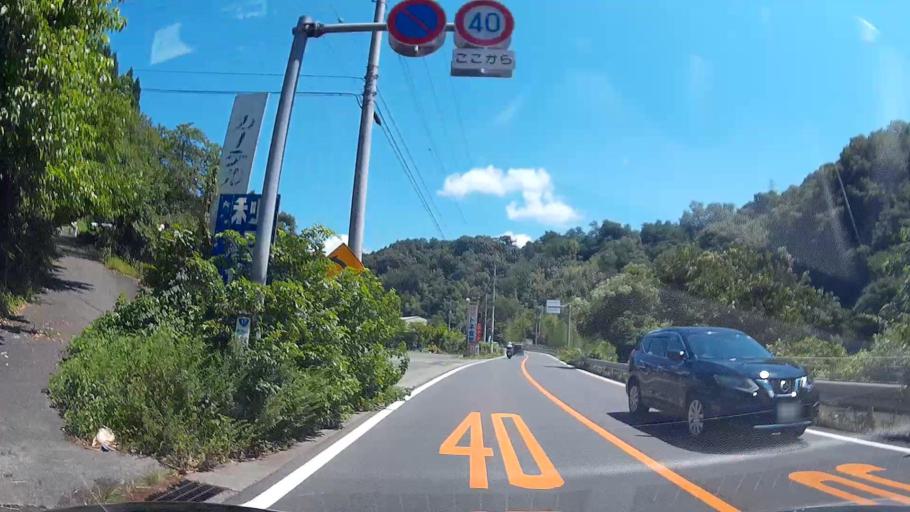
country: JP
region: Gunma
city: Numata
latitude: 36.6274
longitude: 139.0371
